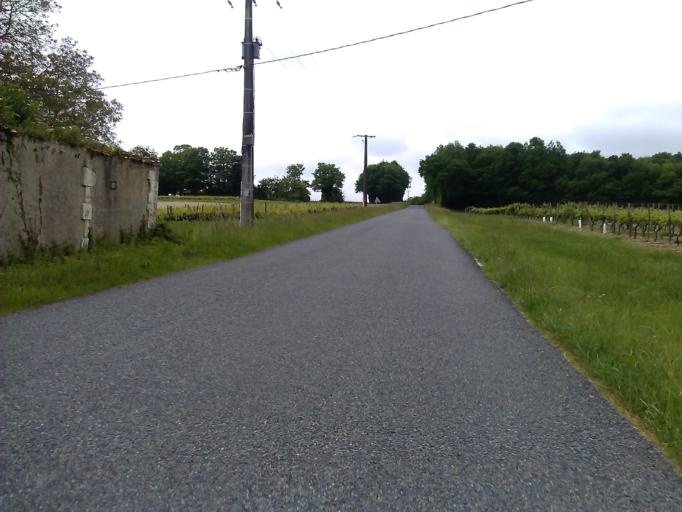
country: FR
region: Poitou-Charentes
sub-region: Departement de la Charente
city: Chateauneuf-sur-Charente
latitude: 45.5467
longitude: -0.0718
